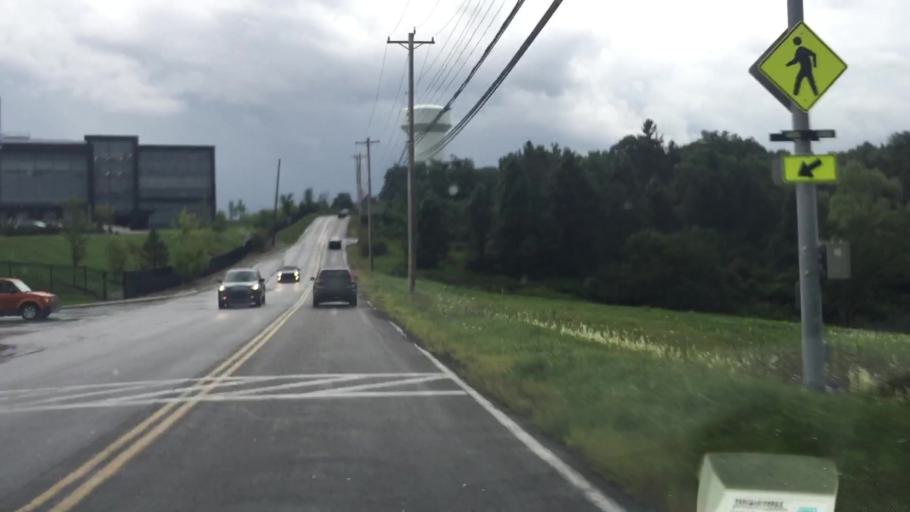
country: US
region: Pennsylvania
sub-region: Allegheny County
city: Rennerdale
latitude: 40.4406
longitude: -80.1615
